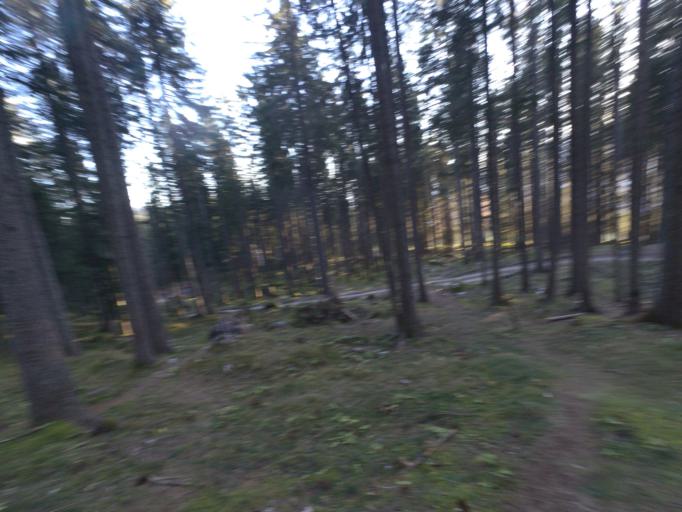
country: AT
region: Salzburg
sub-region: Politischer Bezirk Sankt Johann im Pongau
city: Werfenweng
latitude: 47.4825
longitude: 13.2238
